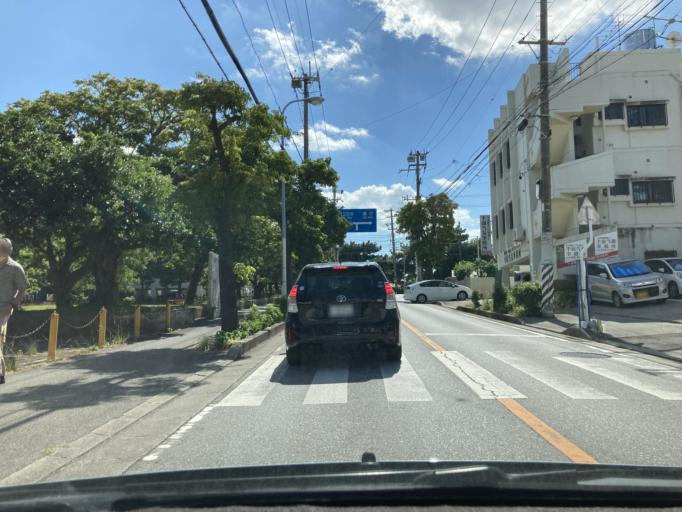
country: JP
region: Okinawa
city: Naha-shi
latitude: 26.2071
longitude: 127.6860
